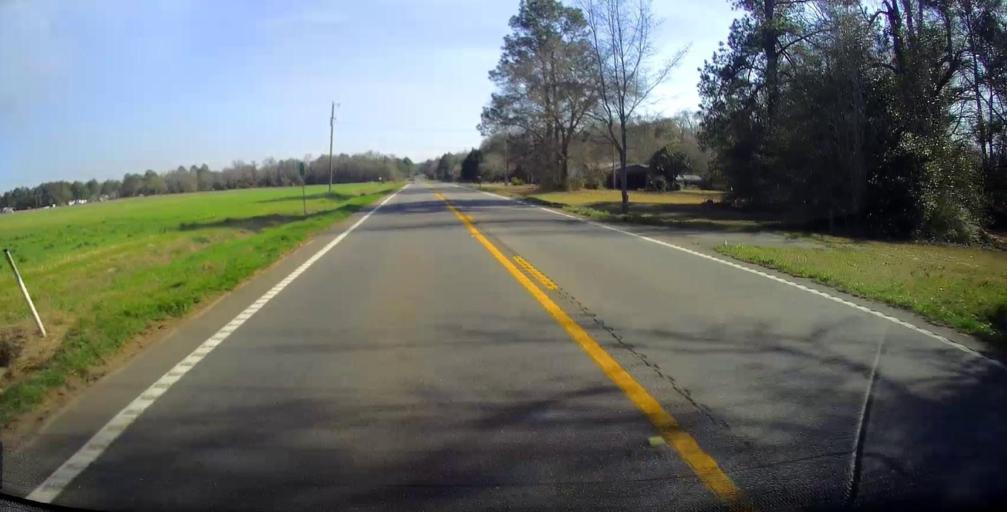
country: US
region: Georgia
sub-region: Macon County
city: Oglethorpe
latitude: 32.3251
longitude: -84.0706
